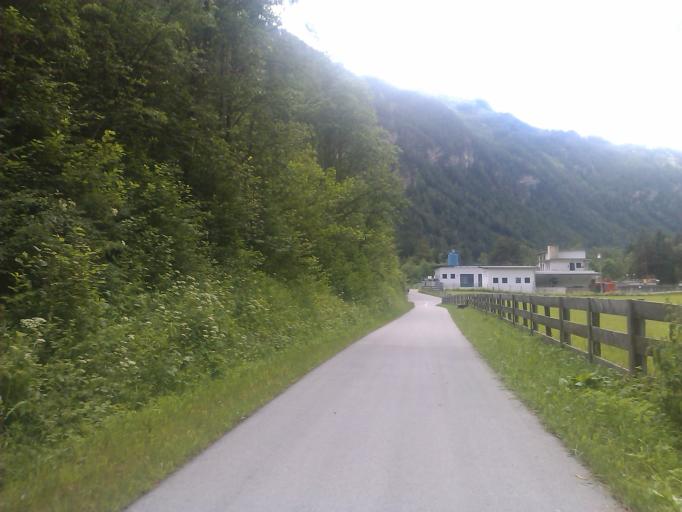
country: AT
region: Tyrol
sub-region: Politischer Bezirk Landeck
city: Fiss
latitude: 47.0376
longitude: 10.6298
